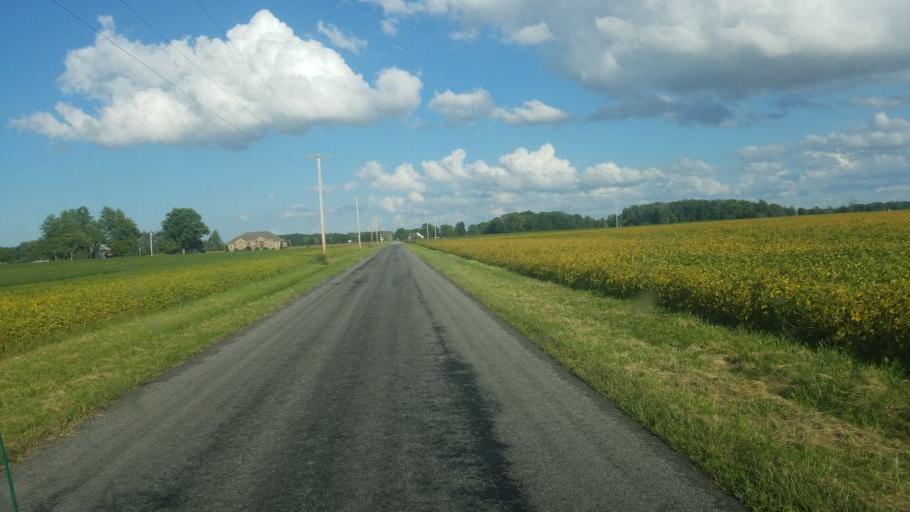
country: US
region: Ohio
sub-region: Hancock County
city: Arlington
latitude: 40.9361
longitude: -83.7017
